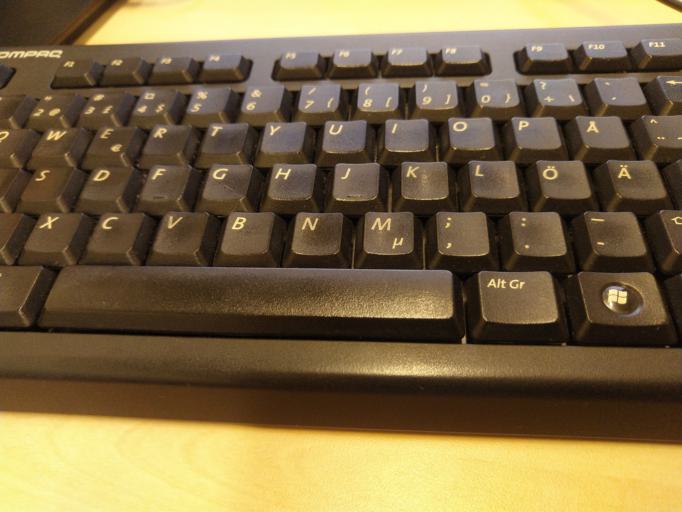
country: FI
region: Northern Ostrobothnia
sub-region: Koillismaa
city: Kuusamo
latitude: 65.9622
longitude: 29.1673
